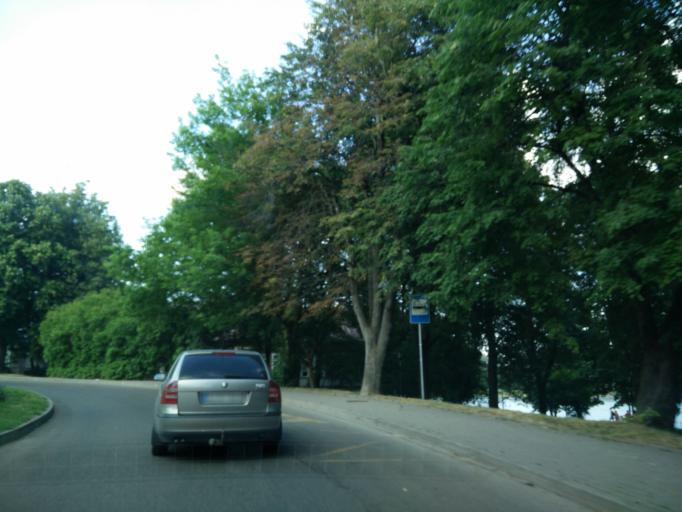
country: LT
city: Trakai
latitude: 54.6444
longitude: 24.9357
